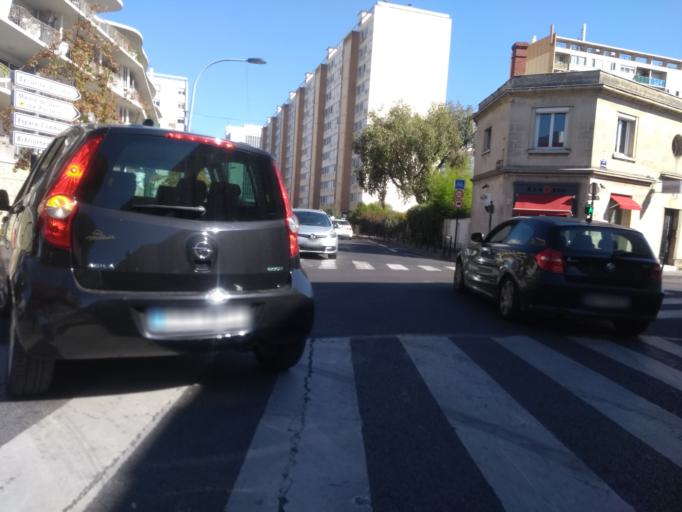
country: FR
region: Aquitaine
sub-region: Departement de la Gironde
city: Le Bouscat
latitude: 44.8572
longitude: -0.5869
